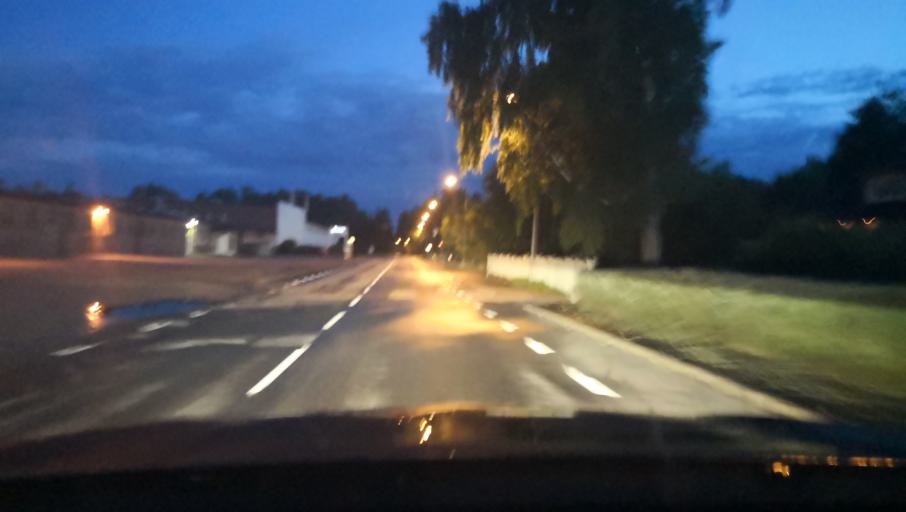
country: SE
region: Skane
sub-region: Hassleholms Kommun
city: Hastveda
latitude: 56.2943
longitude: 13.9432
